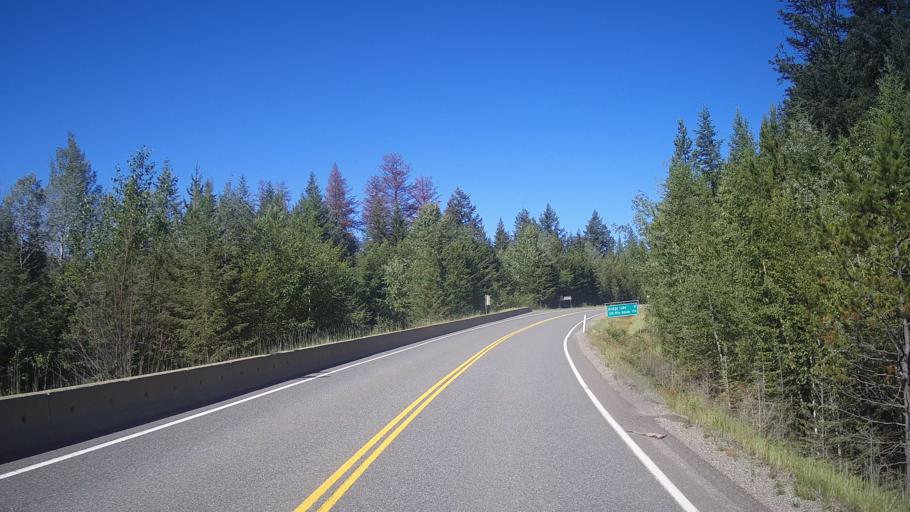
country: CA
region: British Columbia
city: Kamloops
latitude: 51.4724
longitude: -120.5497
